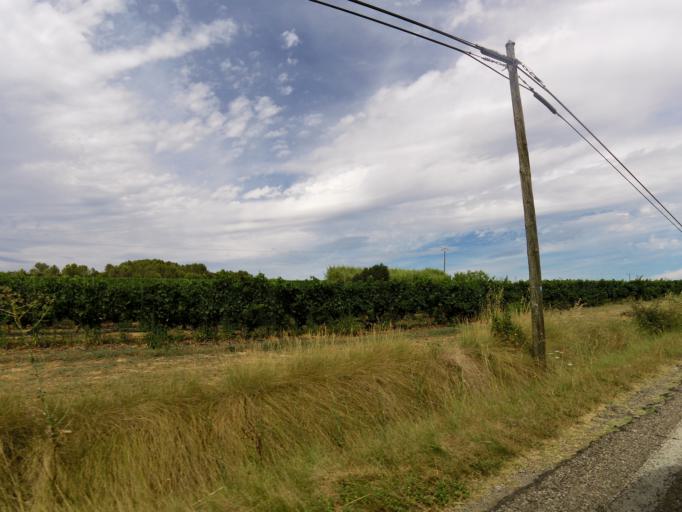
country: FR
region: Languedoc-Roussillon
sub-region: Departement du Gard
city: Villevieille
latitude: 43.8222
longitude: 4.1366
